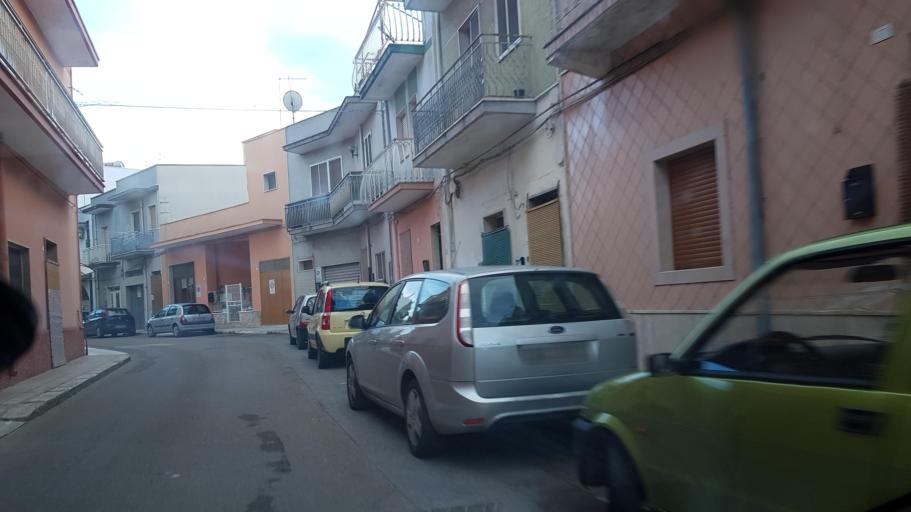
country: IT
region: Apulia
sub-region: Provincia di Brindisi
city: San Vito dei Normanni
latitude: 40.6547
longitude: 17.6991
